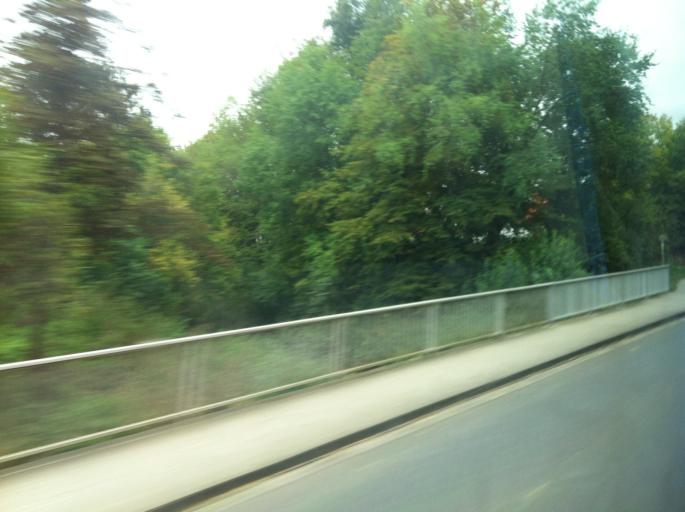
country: DE
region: Rheinland-Pfalz
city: Stadecken-Elsheim
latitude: 49.9118
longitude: 8.1253
